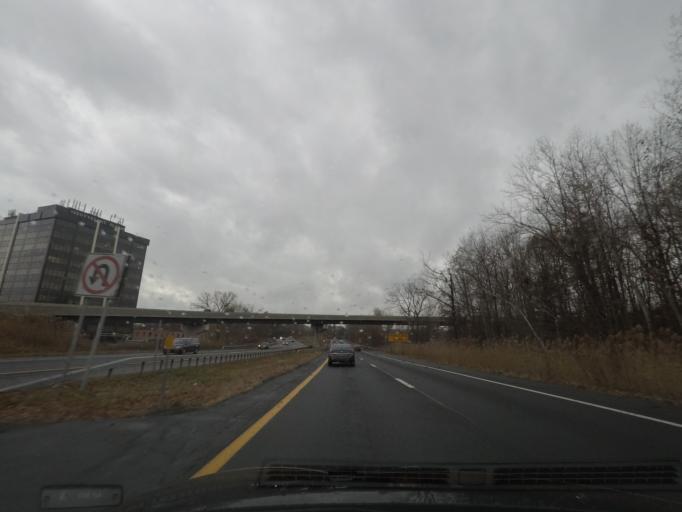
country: US
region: New York
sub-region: Albany County
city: McKownville
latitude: 42.6874
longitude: -73.8434
